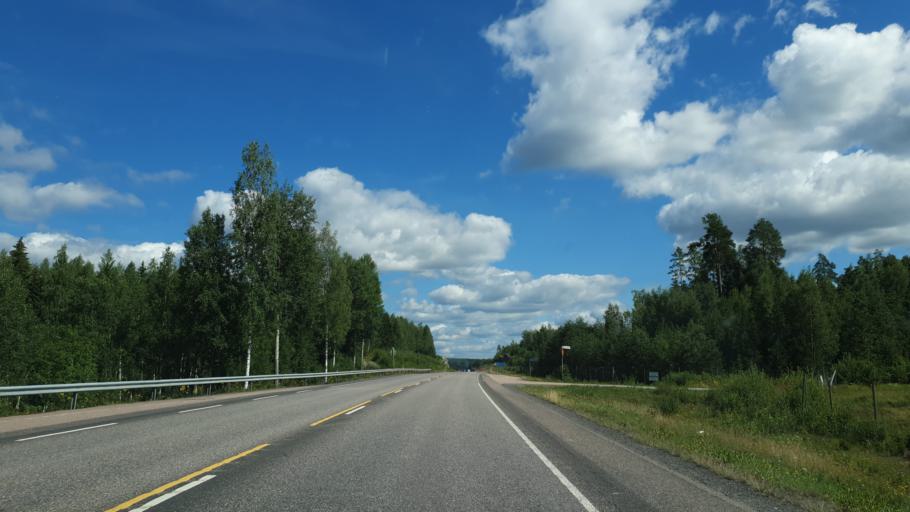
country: FI
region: Pirkanmaa
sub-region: Tampere
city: Orivesi
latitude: 61.7082
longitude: 24.4599
